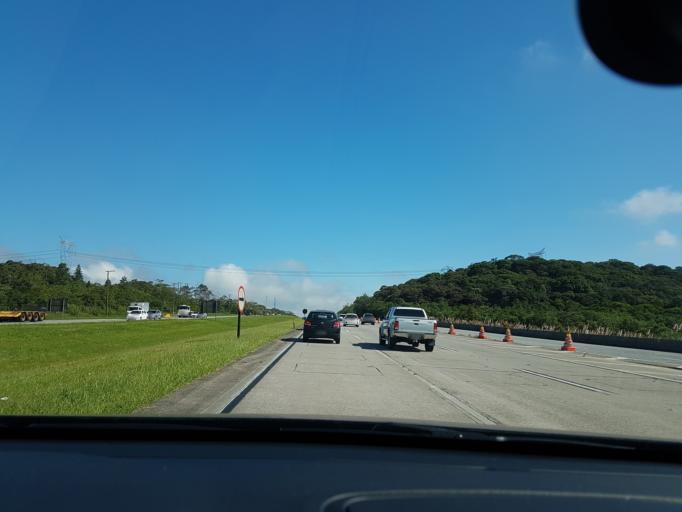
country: BR
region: Sao Paulo
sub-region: Cubatao
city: Cubatao
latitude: -23.8994
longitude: -46.5621
